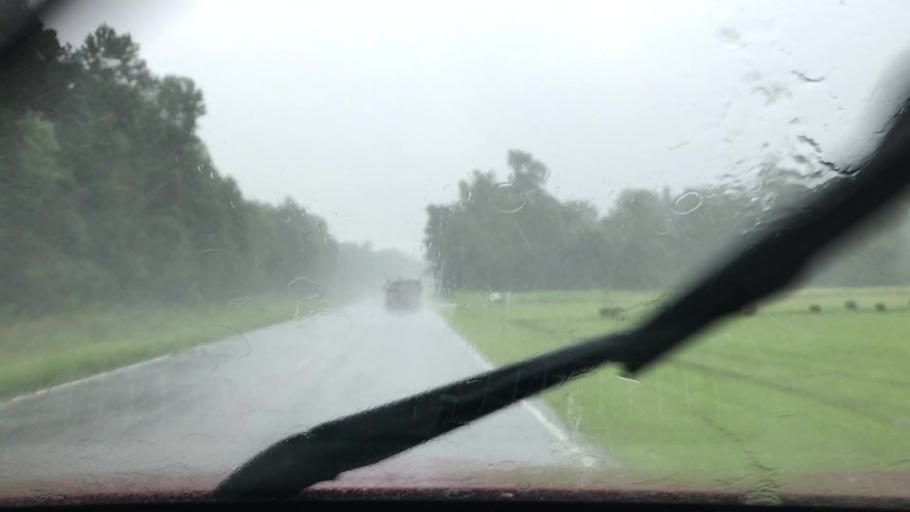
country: US
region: South Carolina
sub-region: Horry County
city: Red Hill
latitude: 33.9025
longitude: -78.9165
